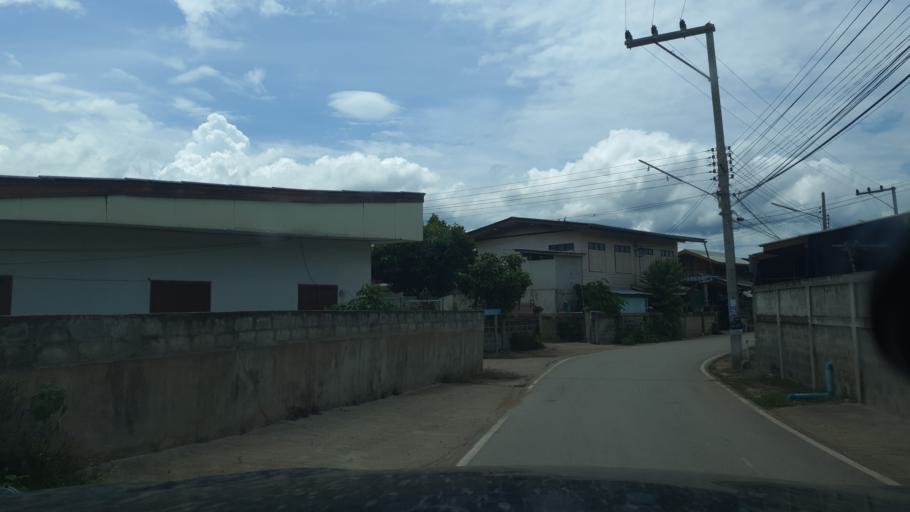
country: TH
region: Lampang
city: Sop Prap
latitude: 17.8808
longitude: 99.3831
